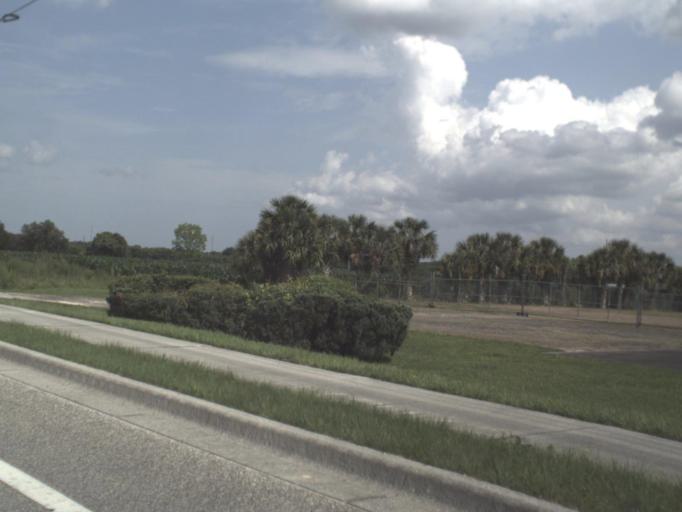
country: US
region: Florida
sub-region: Putnam County
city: East Palatka
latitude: 29.7143
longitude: -81.4990
